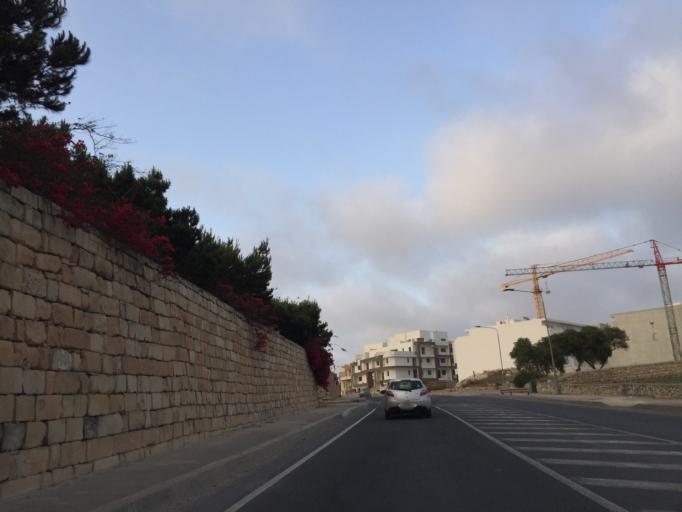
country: MT
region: Il-Mosta
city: Mosta
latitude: 35.9105
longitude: 14.4121
